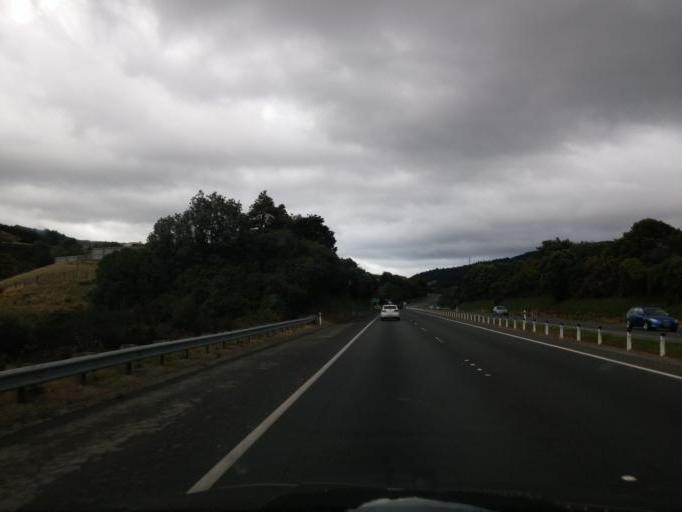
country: NZ
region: Wellington
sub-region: Porirua City
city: Porirua
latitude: -41.1738
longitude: 174.8308
